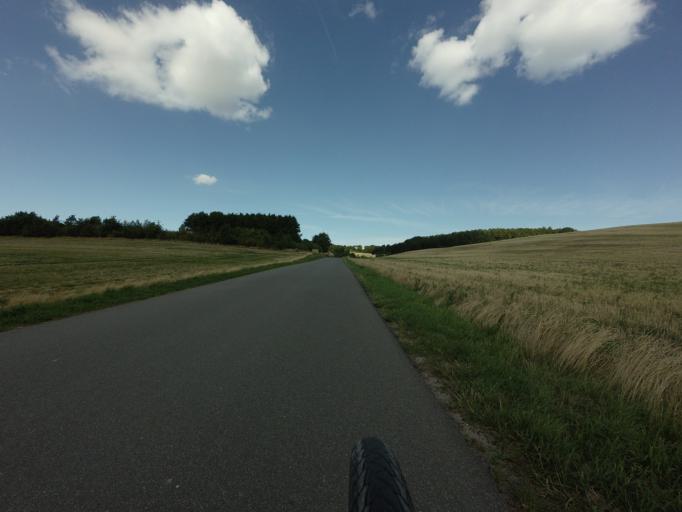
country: DK
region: Zealand
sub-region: Vordingborg Kommune
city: Stege
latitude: 54.9548
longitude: 12.5330
